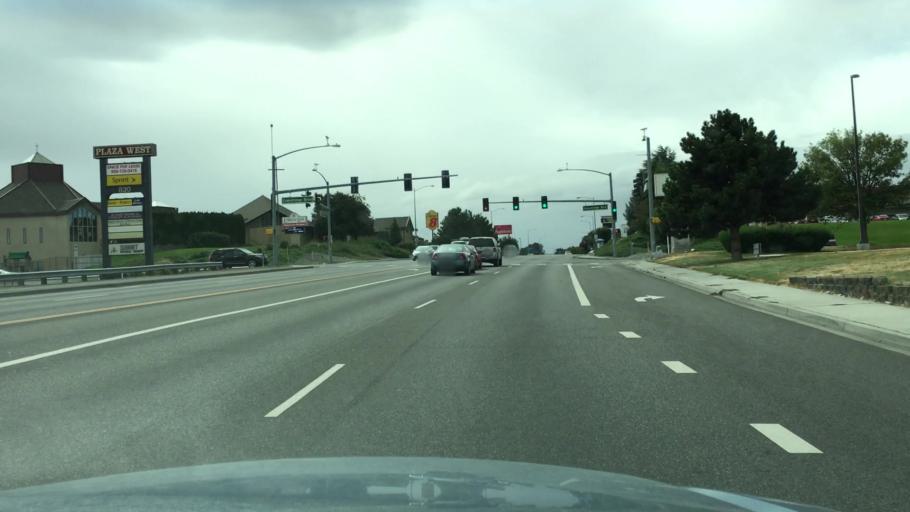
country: US
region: Washington
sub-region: Franklin County
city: West Pasco
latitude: 46.2190
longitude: -119.2243
